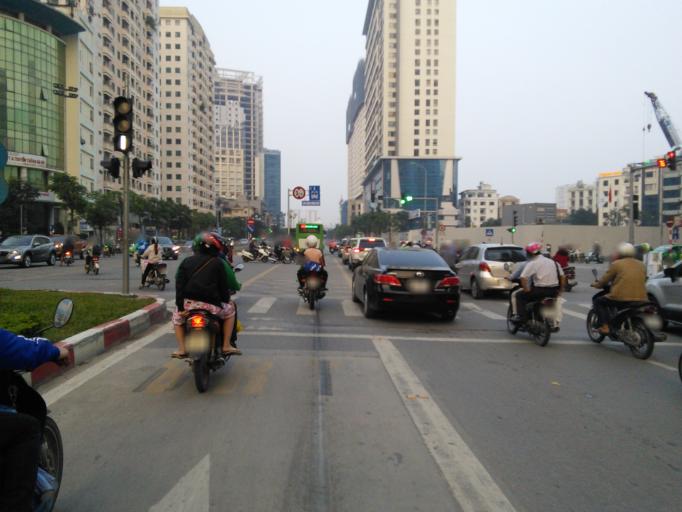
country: VN
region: Ha Noi
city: Thanh Xuan
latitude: 21.0052
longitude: 105.8046
